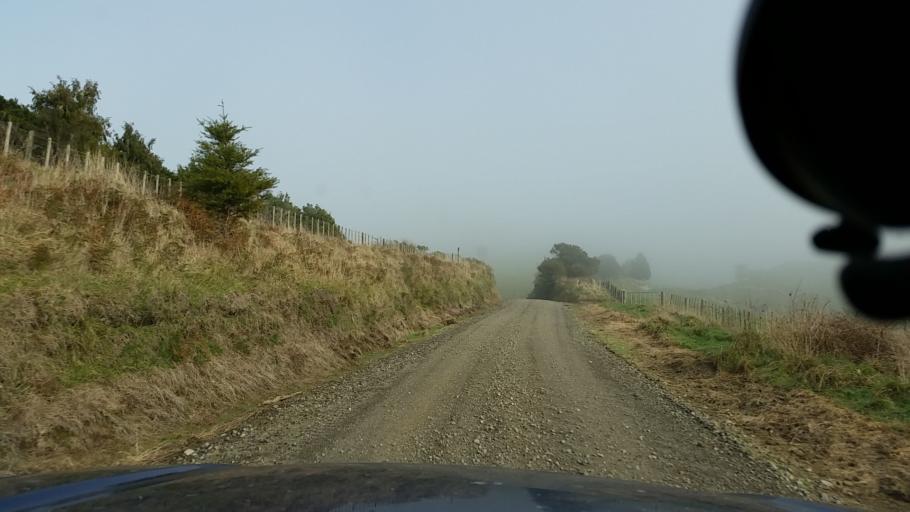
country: NZ
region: Taranaki
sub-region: New Plymouth District
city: Waitara
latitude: -38.9988
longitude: 174.7693
